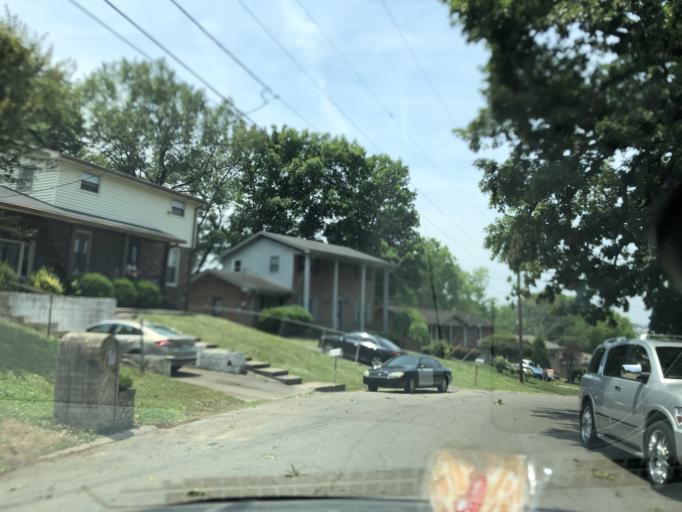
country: US
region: Tennessee
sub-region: Rutherford County
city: La Vergne
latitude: 36.0727
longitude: -86.6727
